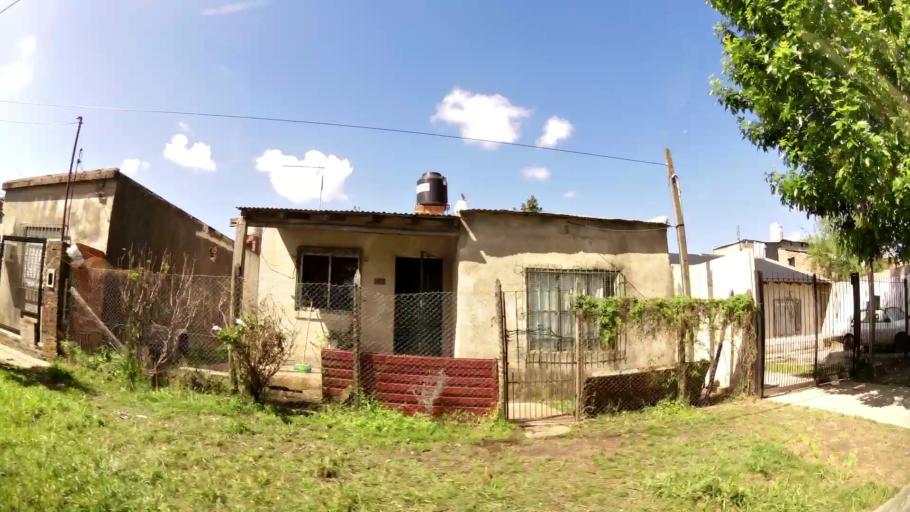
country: AR
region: Buenos Aires
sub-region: Partido de Quilmes
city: Quilmes
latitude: -34.8175
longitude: -58.2647
